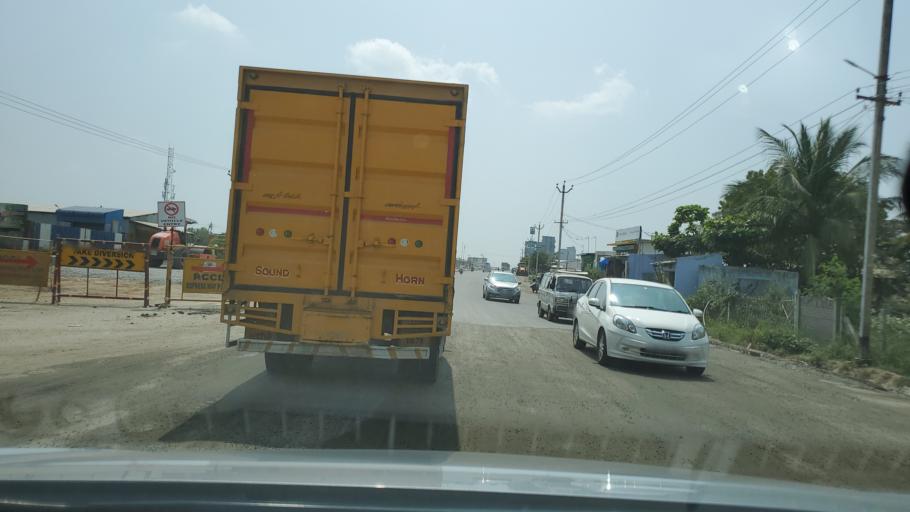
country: IN
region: Tamil Nadu
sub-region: Tiruppur
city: Dharapuram
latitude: 10.7436
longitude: 77.5189
